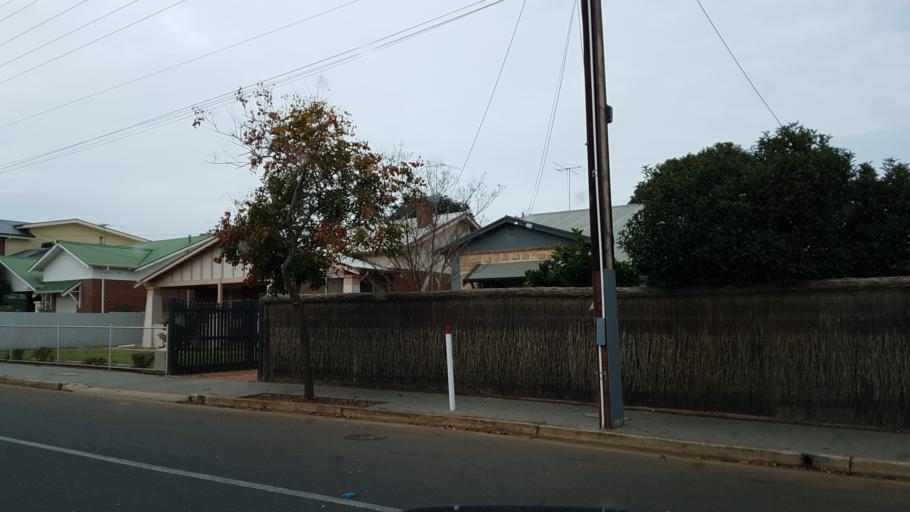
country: AU
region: South Australia
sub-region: Mitcham
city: Hawthorn
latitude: -34.9740
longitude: 138.6116
